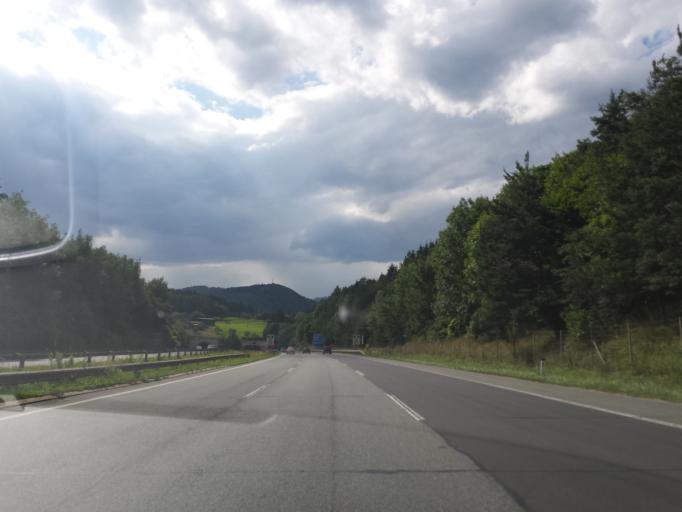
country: AT
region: Styria
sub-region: Politischer Bezirk Graz-Umgebung
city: Gratkorn
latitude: 47.1393
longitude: 15.3509
